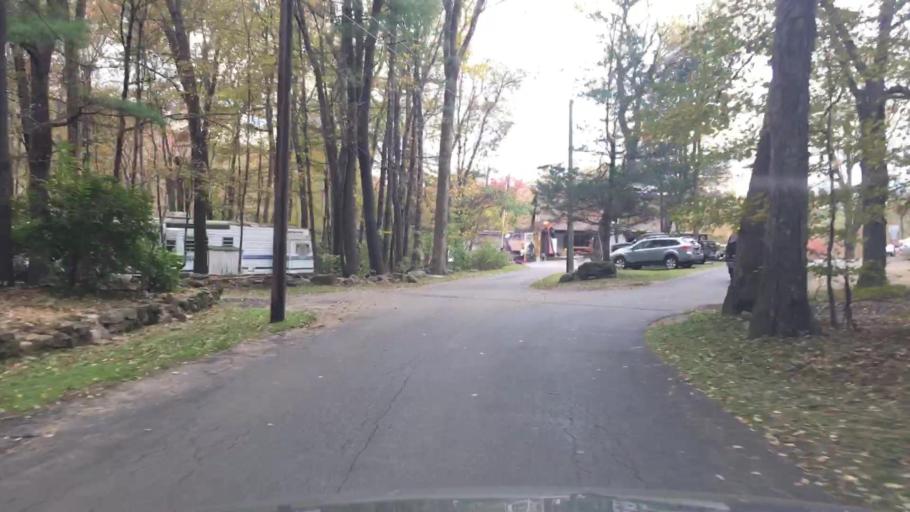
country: US
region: Connecticut
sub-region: Tolland County
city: Storrs
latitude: 41.8865
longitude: -72.1778
